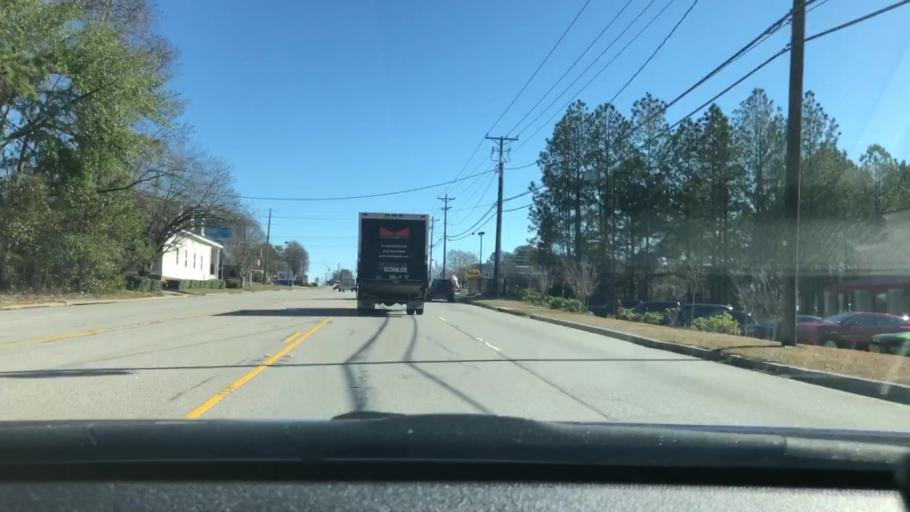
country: US
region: South Carolina
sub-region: Lexington County
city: Oak Grove
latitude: 34.0055
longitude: -81.1191
